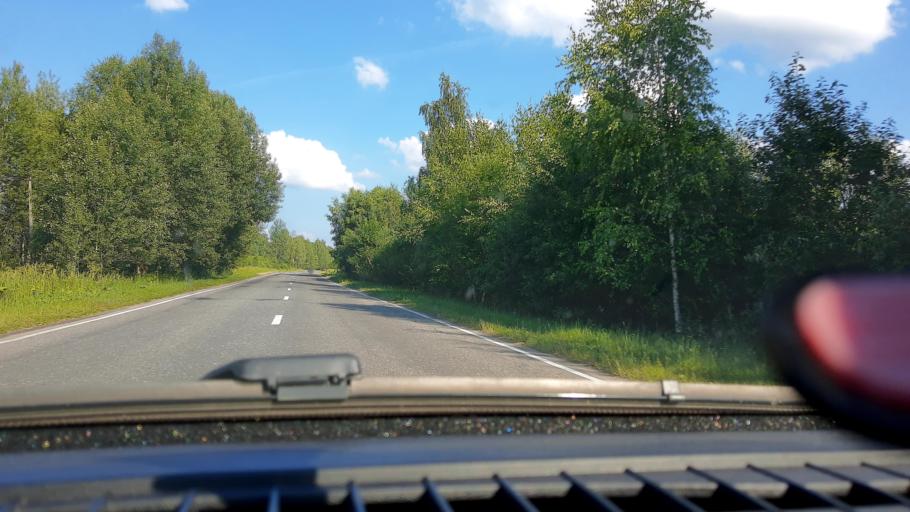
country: RU
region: Nizjnij Novgorod
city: Neklyudovo
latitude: 56.5106
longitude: 43.9553
